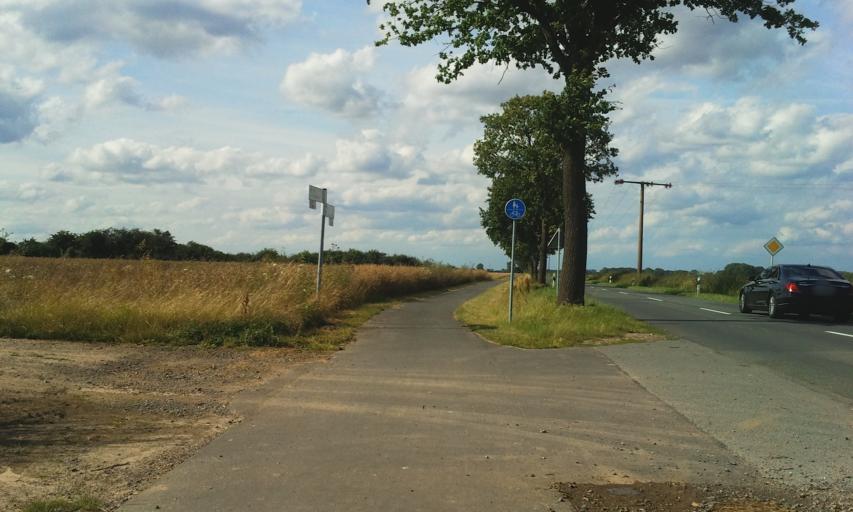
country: DE
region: Lower Saxony
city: Drakenburg
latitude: 52.6917
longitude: 9.2107
